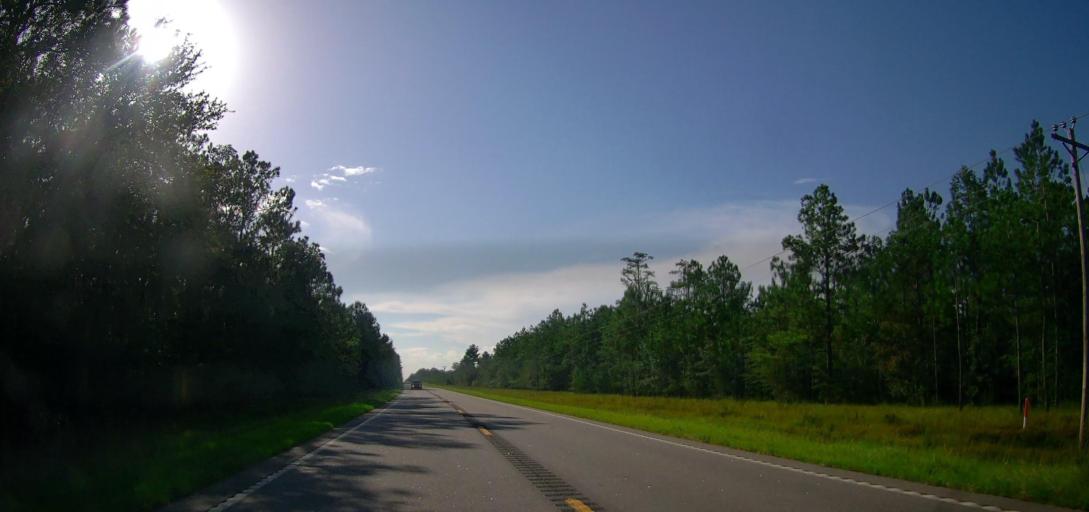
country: US
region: Georgia
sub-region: Coffee County
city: Nicholls
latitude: 31.4550
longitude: -82.7346
